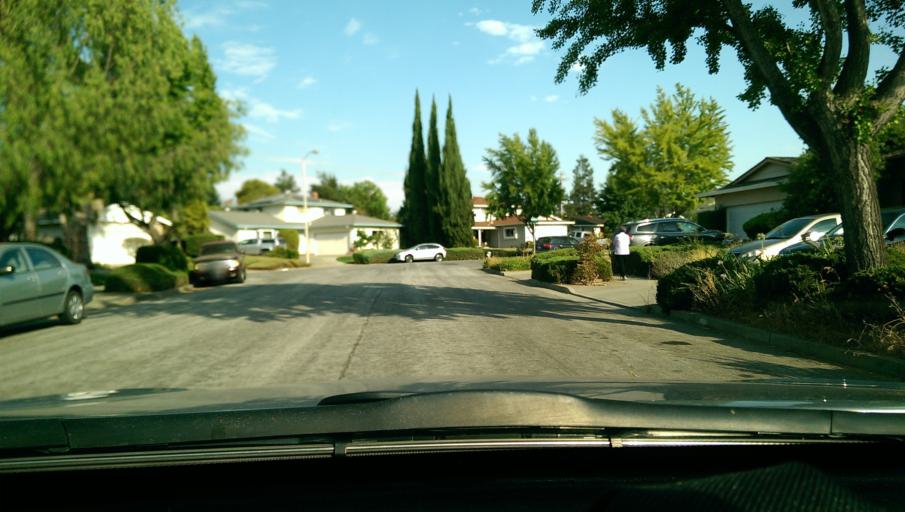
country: US
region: California
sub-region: Santa Clara County
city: Cupertino
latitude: 37.3338
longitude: -122.0191
